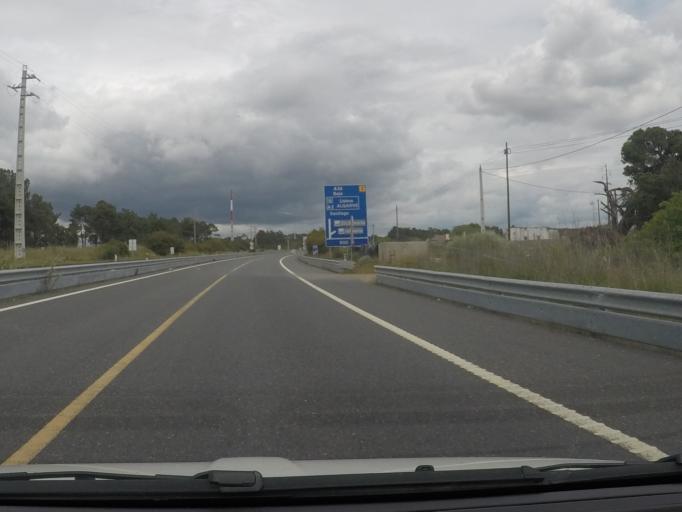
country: PT
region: Setubal
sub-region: Sines
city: Sines
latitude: 37.9729
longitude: -8.8204
